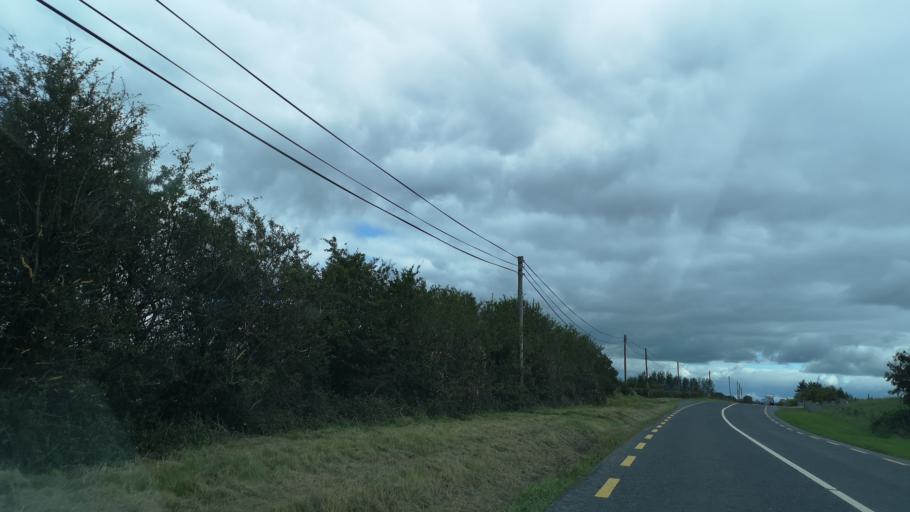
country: IE
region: Connaught
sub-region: County Galway
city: Ballinasloe
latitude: 53.3061
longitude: -8.1432
